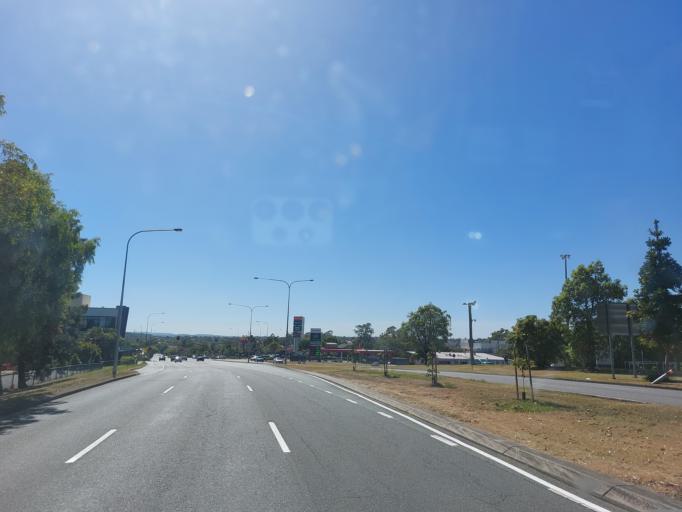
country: AU
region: Queensland
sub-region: Brisbane
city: Sunnybank Hills
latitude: -27.6112
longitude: 153.0524
